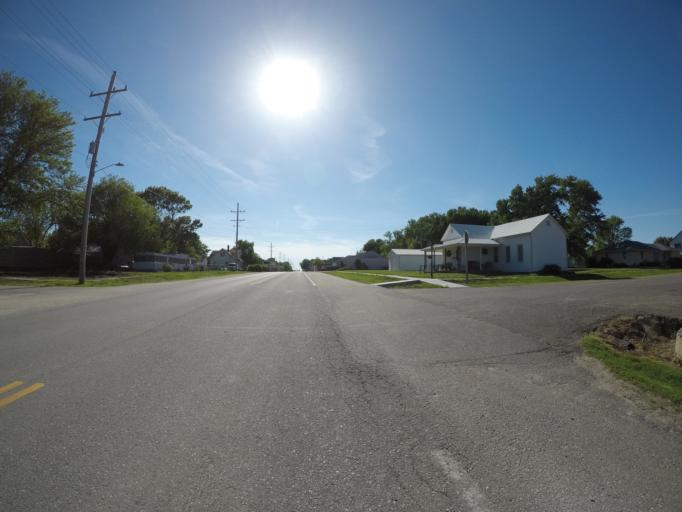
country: US
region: Kansas
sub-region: Riley County
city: Fort Riley North
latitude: 39.3644
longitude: -96.8560
